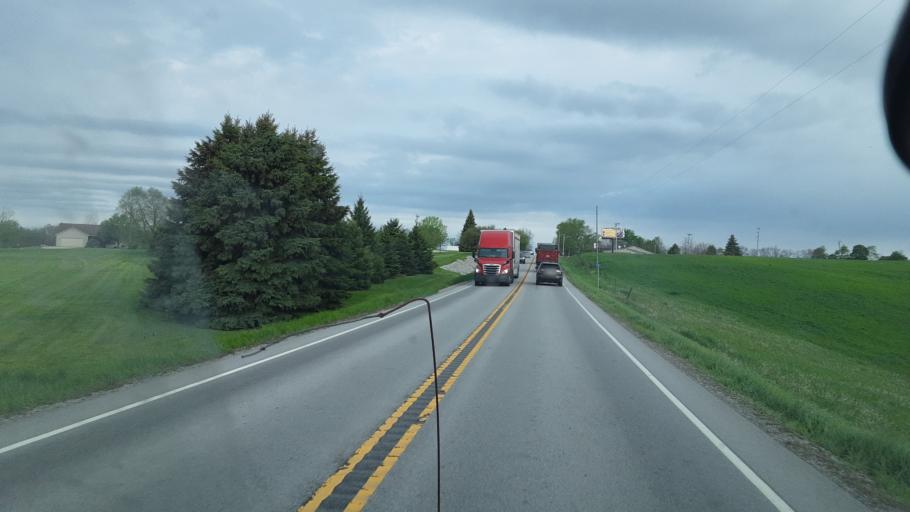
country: US
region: Indiana
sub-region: Whitley County
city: Tri-Lakes
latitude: 41.2696
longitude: -85.4024
